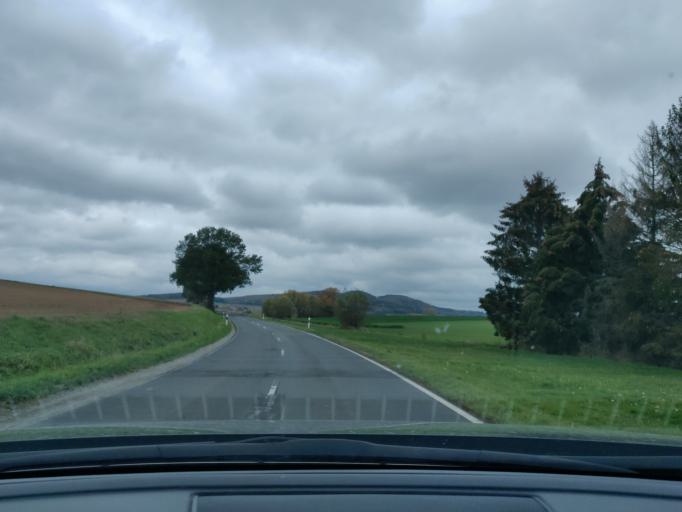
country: DE
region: Hesse
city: Niedenstein
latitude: 51.1850
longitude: 9.3009
